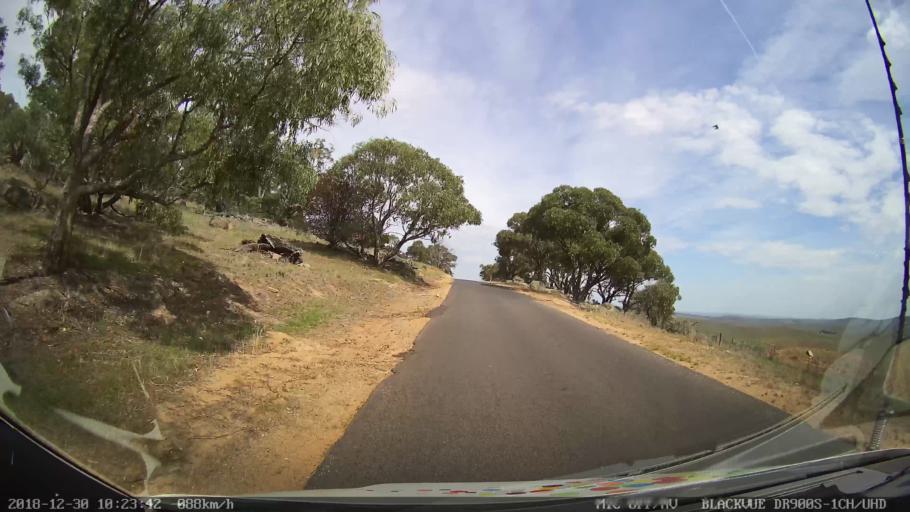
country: AU
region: New South Wales
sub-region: Snowy River
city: Berridale
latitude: -36.5344
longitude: 148.9793
